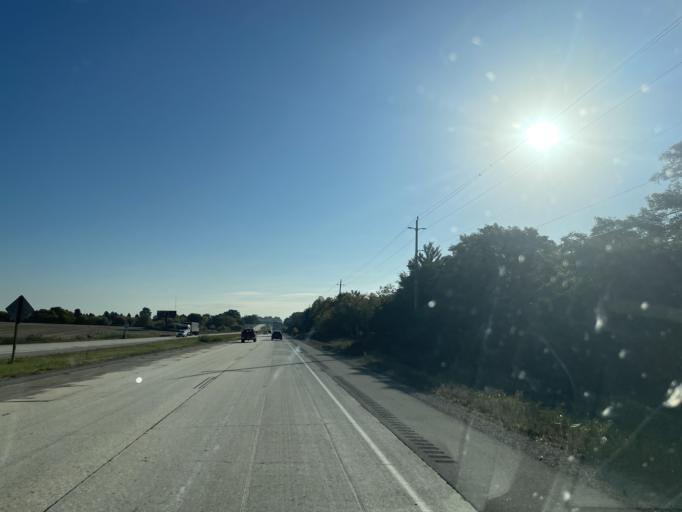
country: US
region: Wisconsin
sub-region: Kenosha County
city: Bristol
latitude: 42.5682
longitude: -88.0399
